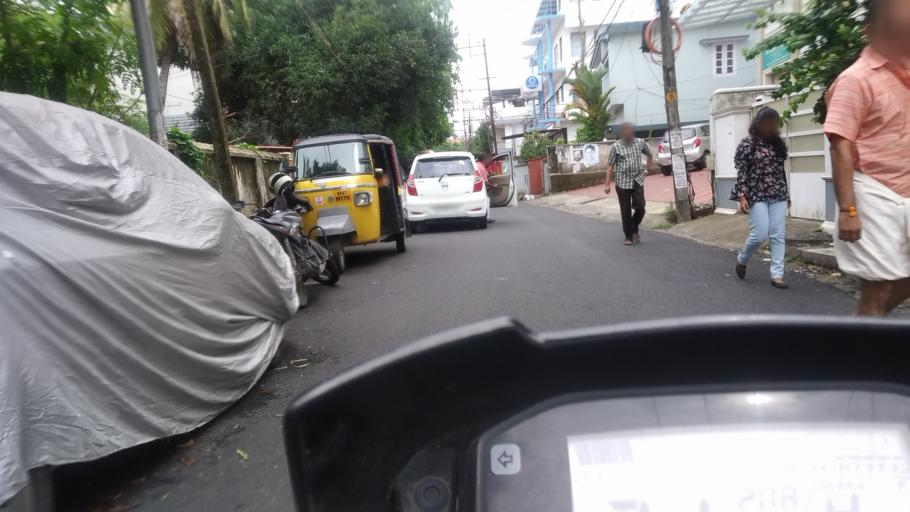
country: IN
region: Kerala
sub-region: Ernakulam
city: Cochin
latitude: 9.9941
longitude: 76.2792
